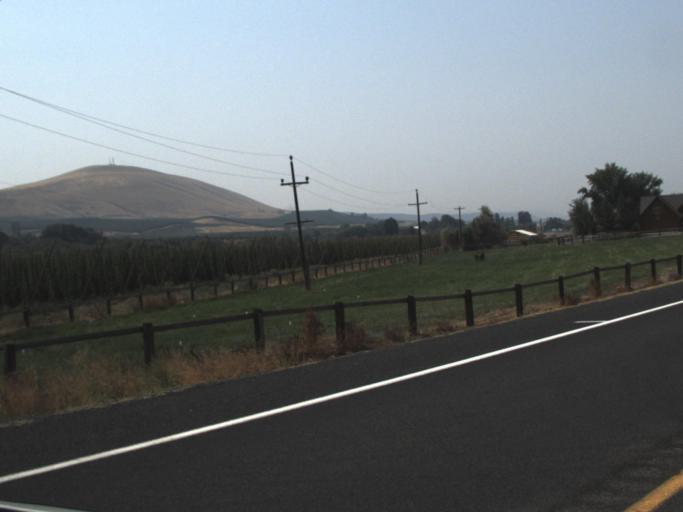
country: US
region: Washington
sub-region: Yakima County
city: Zillah
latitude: 46.5350
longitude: -120.2924
